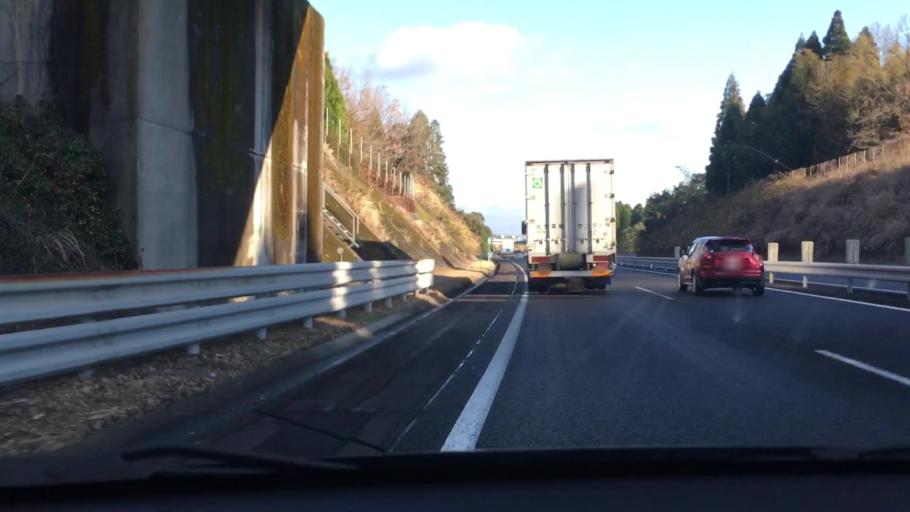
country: JP
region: Kagoshima
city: Kajiki
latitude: 31.8196
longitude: 130.6980
